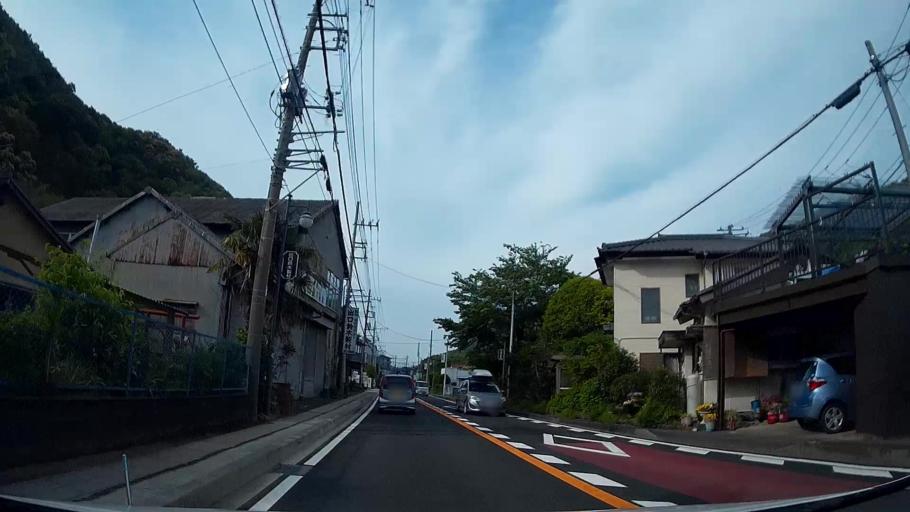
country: JP
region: Shizuoka
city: Heda
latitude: 34.9298
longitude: 138.9332
